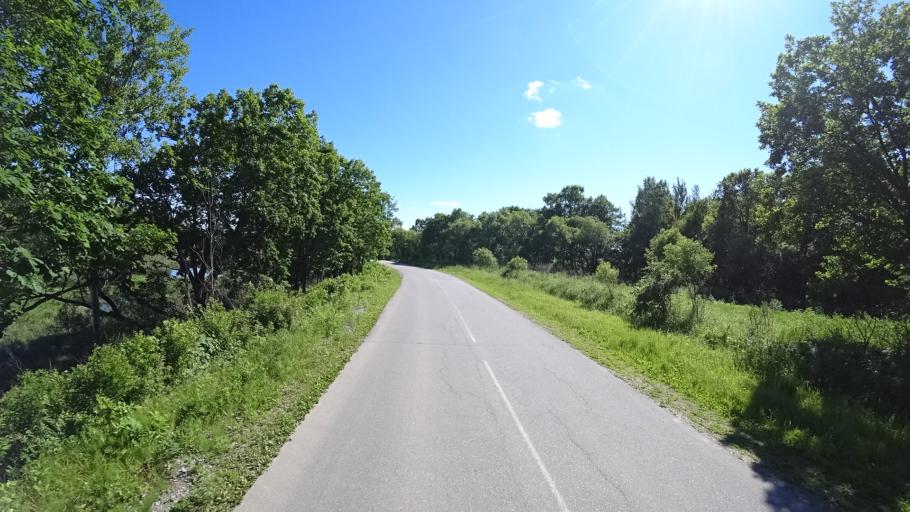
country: RU
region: Khabarovsk Krai
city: Khor
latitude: 47.8937
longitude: 135.0229
